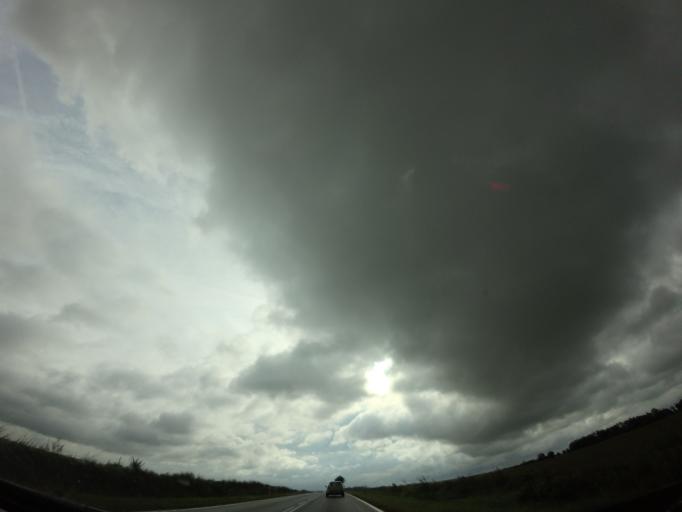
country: PL
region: Greater Poland Voivodeship
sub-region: Powiat pilski
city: Osiek nad Notecia
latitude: 53.1549
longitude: 17.3602
